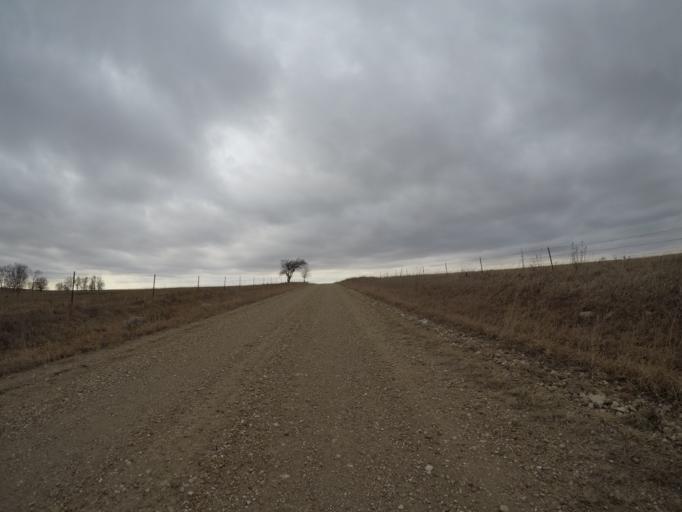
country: US
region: Kansas
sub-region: Wabaunsee County
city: Alma
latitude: 38.7245
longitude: -96.1738
